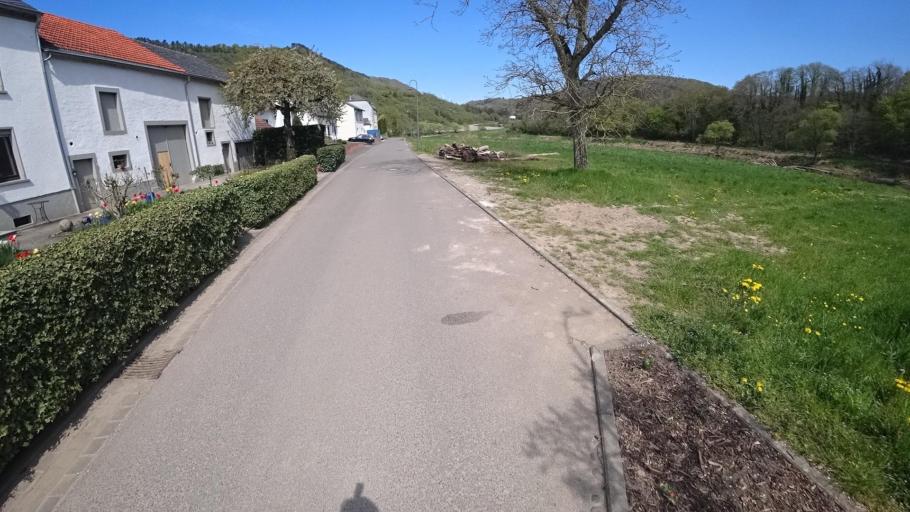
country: LU
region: Grevenmacher
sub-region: Canton d'Echternach
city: Rosport
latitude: 49.8080
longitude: 6.5165
